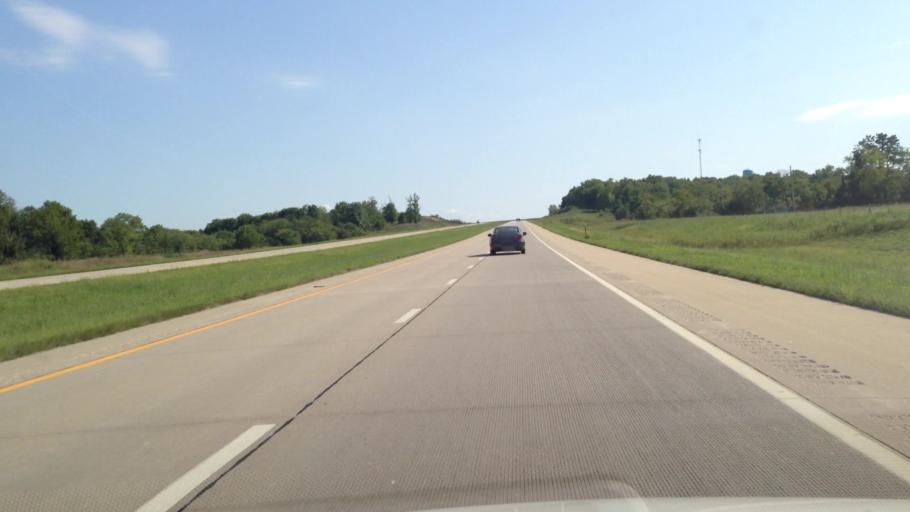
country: US
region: Kansas
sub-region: Linn County
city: Pleasanton
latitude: 38.1216
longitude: -94.7137
